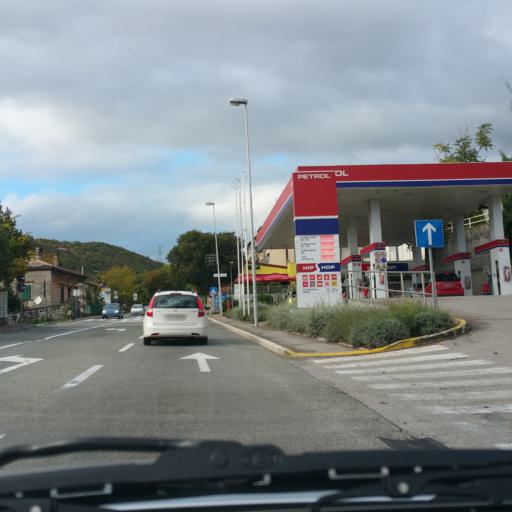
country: HR
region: Primorsko-Goranska
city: Drenova
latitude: 45.3414
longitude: 14.4254
